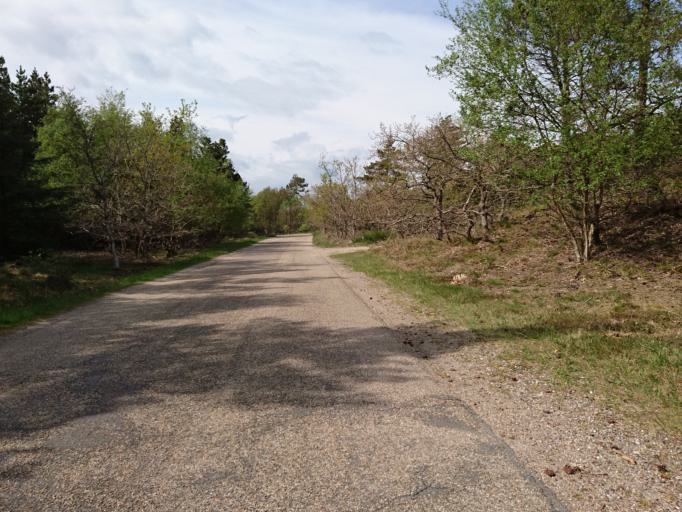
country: DK
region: North Denmark
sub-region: Frederikshavn Kommune
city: Skagen
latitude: 57.7172
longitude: 10.5426
